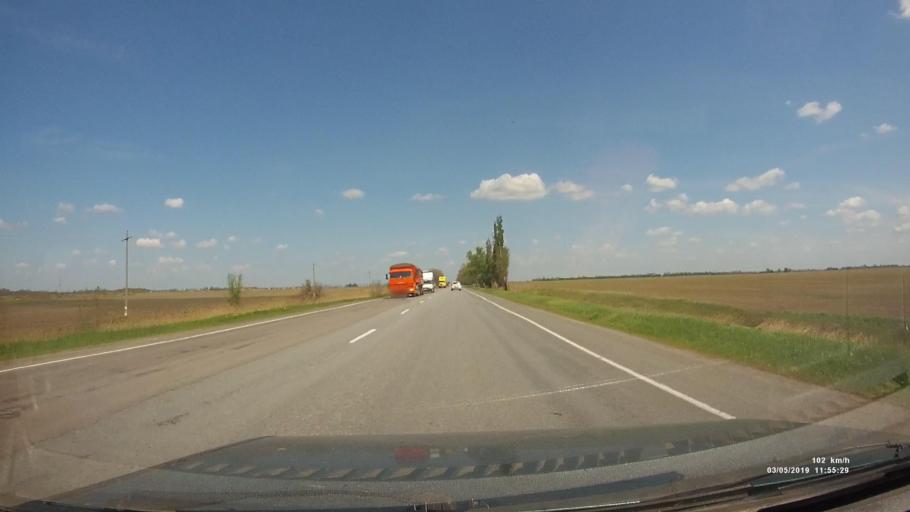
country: RU
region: Rostov
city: Bagayevskaya
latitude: 47.1817
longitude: 40.2916
